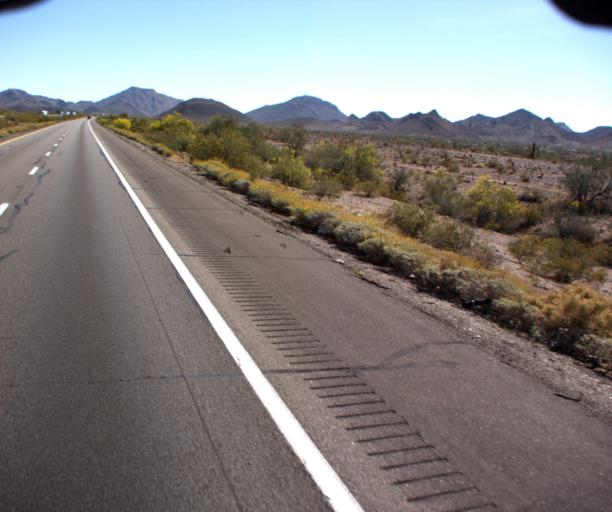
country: US
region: Arizona
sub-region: La Paz County
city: Quartzsite
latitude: 33.6771
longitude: -114.1179
